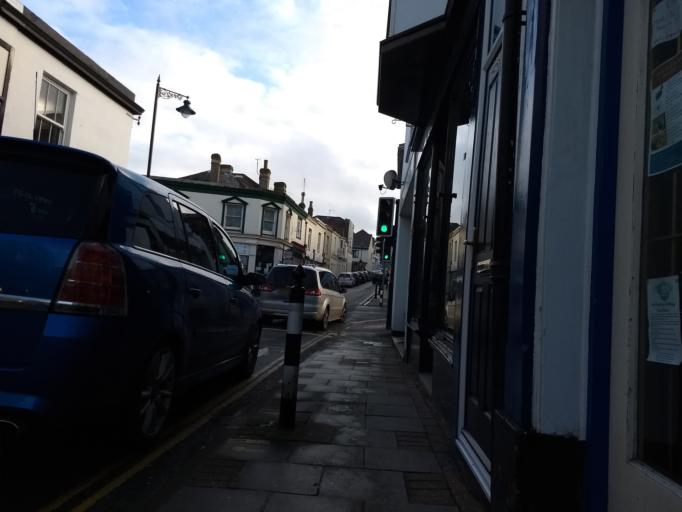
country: GB
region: England
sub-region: Isle of Wight
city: Ryde
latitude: 50.7262
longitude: -1.1629
